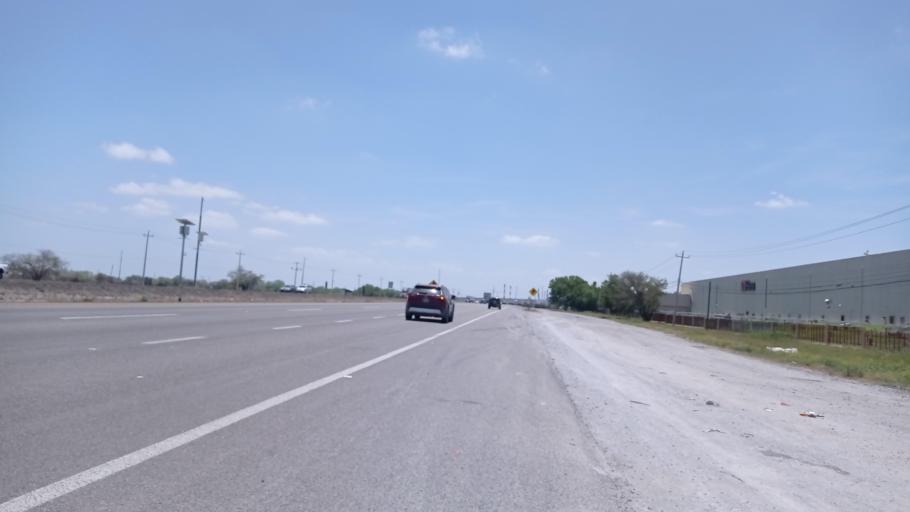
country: MX
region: Nuevo Leon
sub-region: General Zuazua
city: Villas de Alcala
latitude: 25.8918
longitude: -100.2224
